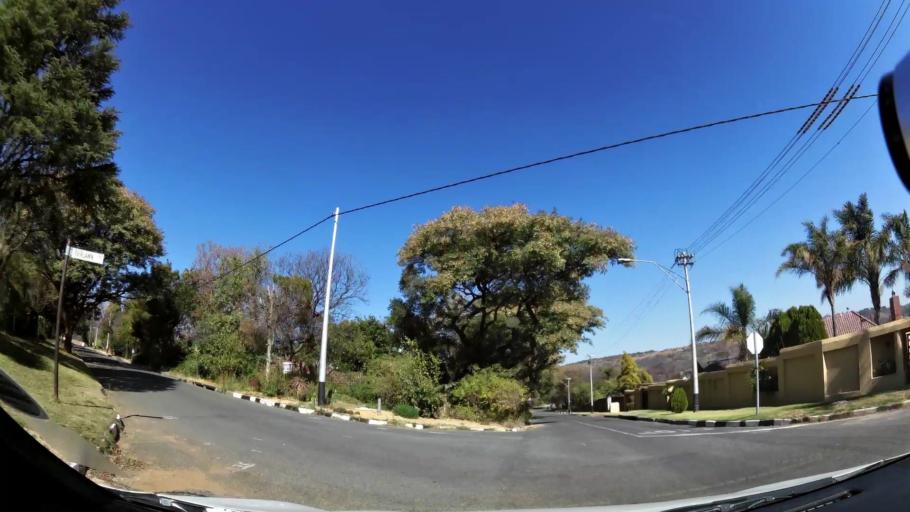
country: ZA
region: Gauteng
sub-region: City of Johannesburg Metropolitan Municipality
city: Johannesburg
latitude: -26.2722
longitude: 28.0123
